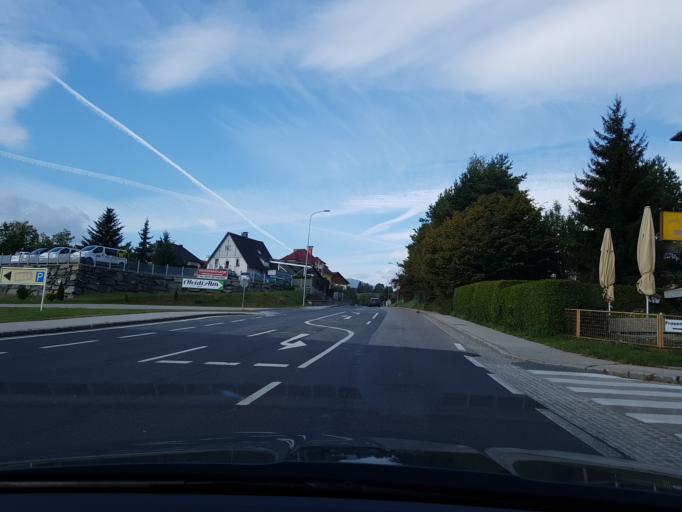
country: AT
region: Carinthia
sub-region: Politischer Bezirk Feldkirchen
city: Feldkirchen in Karnten
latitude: 46.7269
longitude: 14.0888
